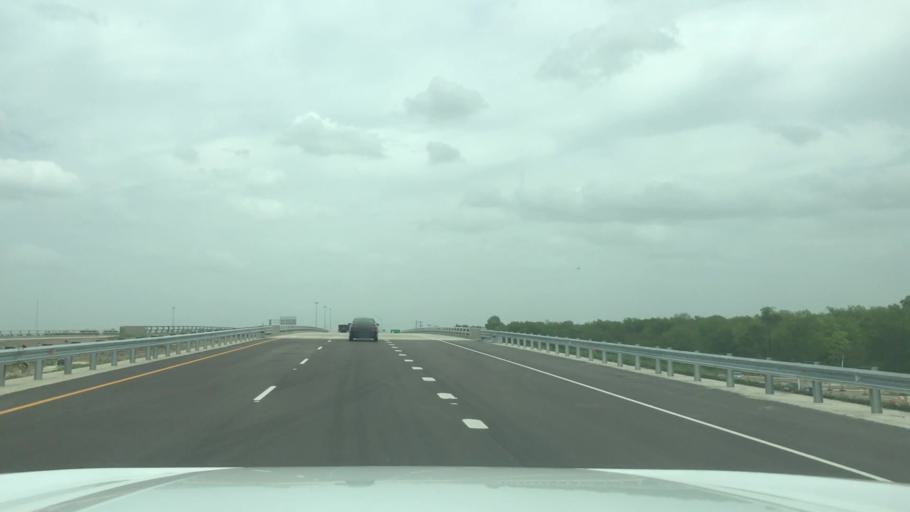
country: US
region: Texas
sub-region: McLennan County
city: Beverly
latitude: 31.4941
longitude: -97.1345
